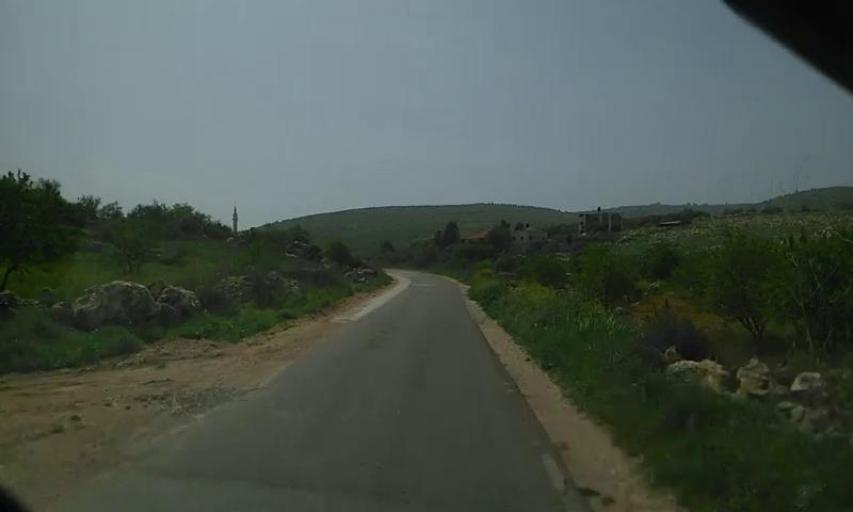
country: PS
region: West Bank
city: At Taybah
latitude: 32.5064
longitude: 35.2004
